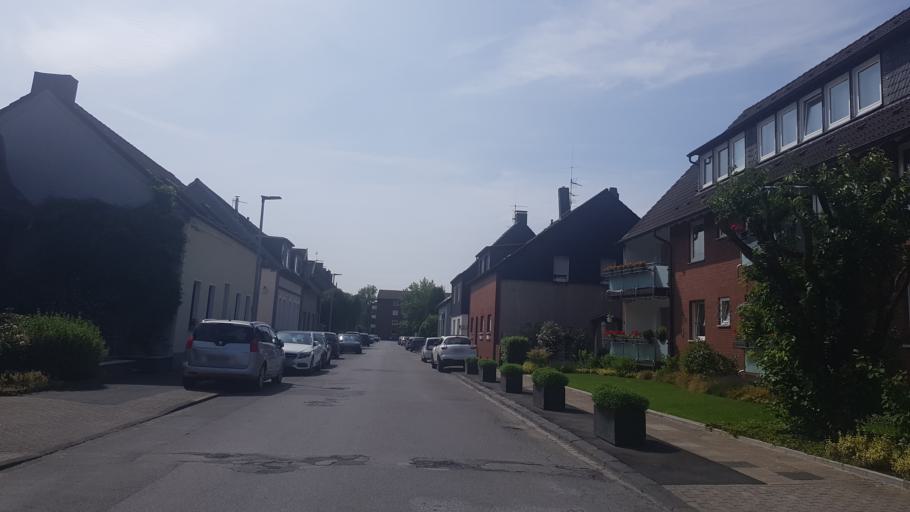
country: DE
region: North Rhine-Westphalia
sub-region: Regierungsbezirk Dusseldorf
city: Oberhausen
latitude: 51.4595
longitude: 6.8654
